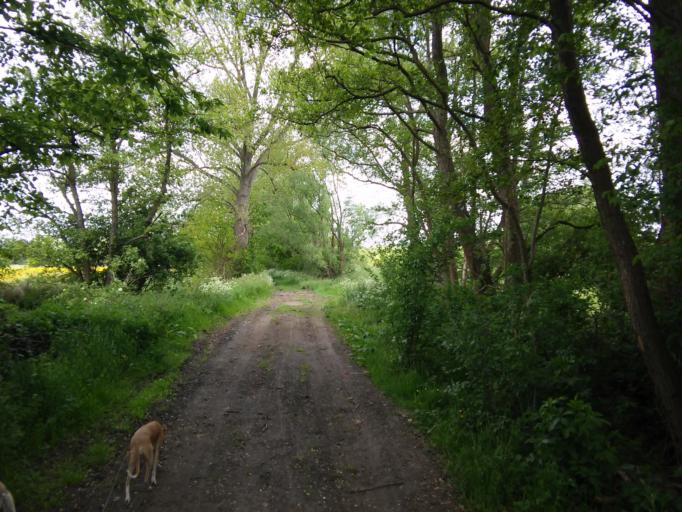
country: BE
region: Flanders
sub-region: Provincie Antwerpen
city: Mechelen
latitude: 51.0304
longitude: 4.4394
